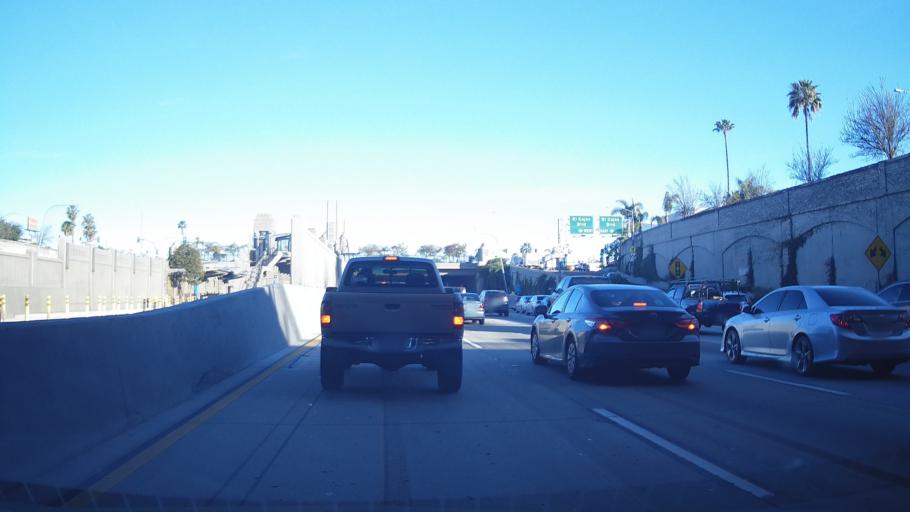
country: US
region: California
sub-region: San Diego County
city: San Diego
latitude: 32.7511
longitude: -117.1106
